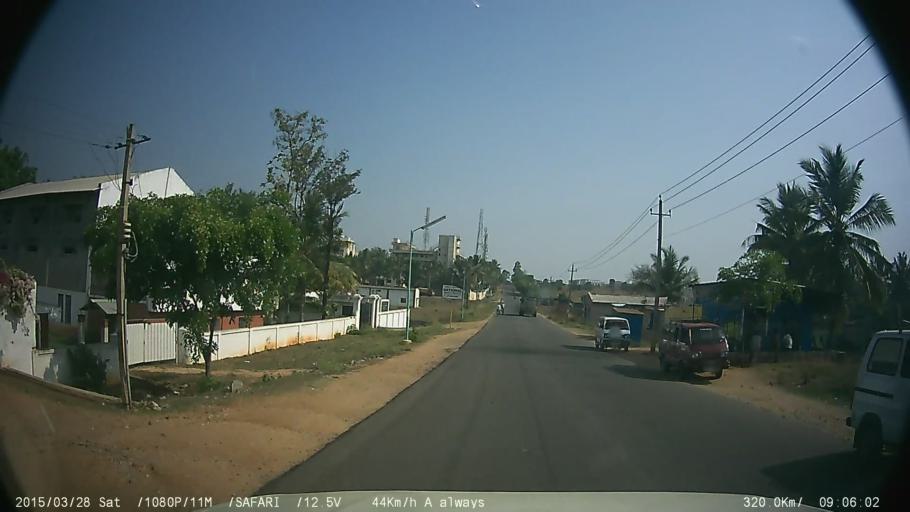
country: IN
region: Karnataka
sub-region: Mysore
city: Mysore
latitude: 12.3527
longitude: 76.5970
